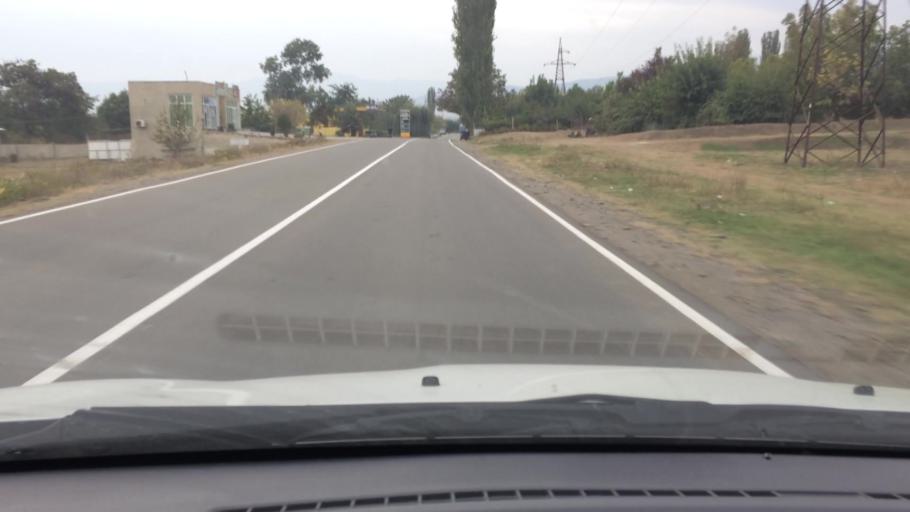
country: GE
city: Naghvarevi
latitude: 41.3289
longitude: 44.8027
